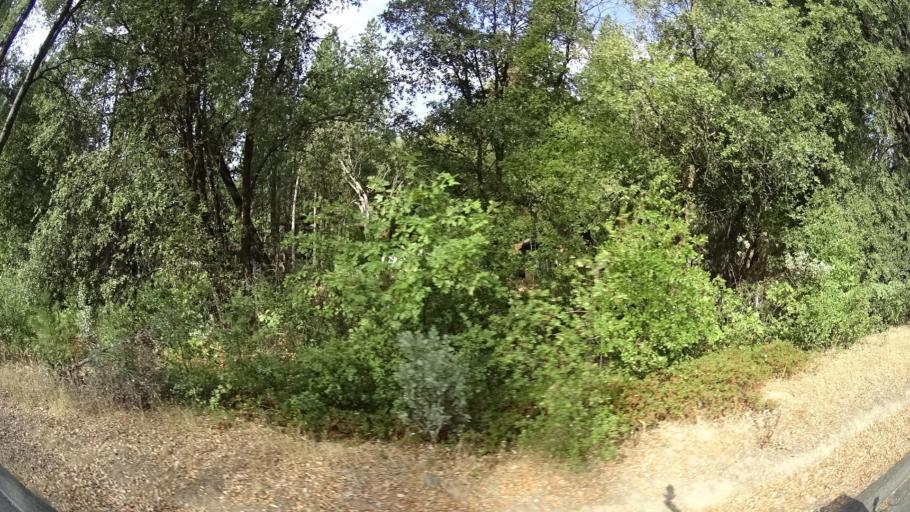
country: US
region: California
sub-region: Madera County
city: Ahwahnee
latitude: 37.4698
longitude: -119.7693
